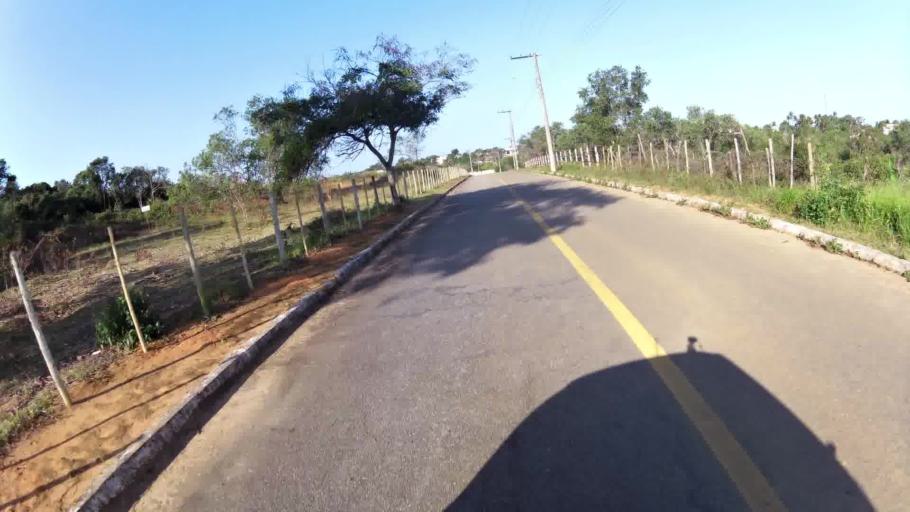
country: BR
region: Espirito Santo
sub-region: Guarapari
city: Guarapari
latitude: -20.7215
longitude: -40.5374
